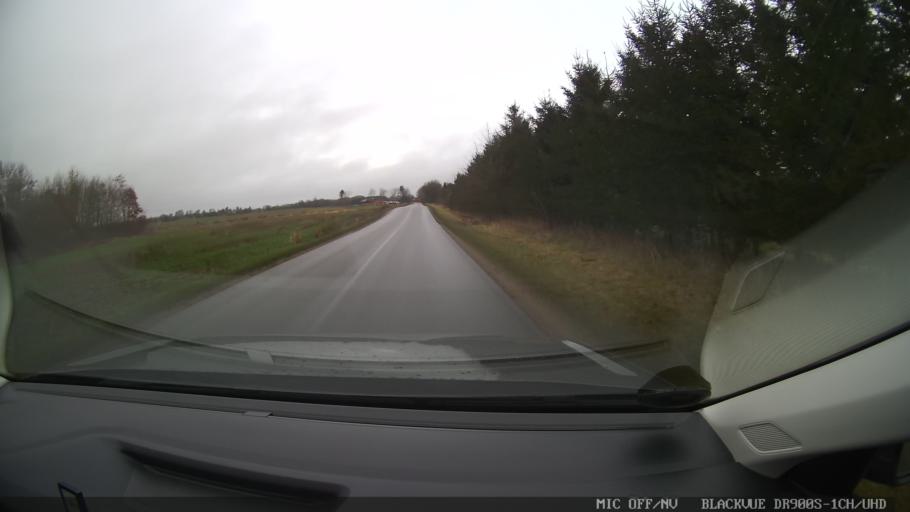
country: DK
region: Central Jutland
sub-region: Viborg Kommune
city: Karup
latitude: 56.3477
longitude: 9.2863
